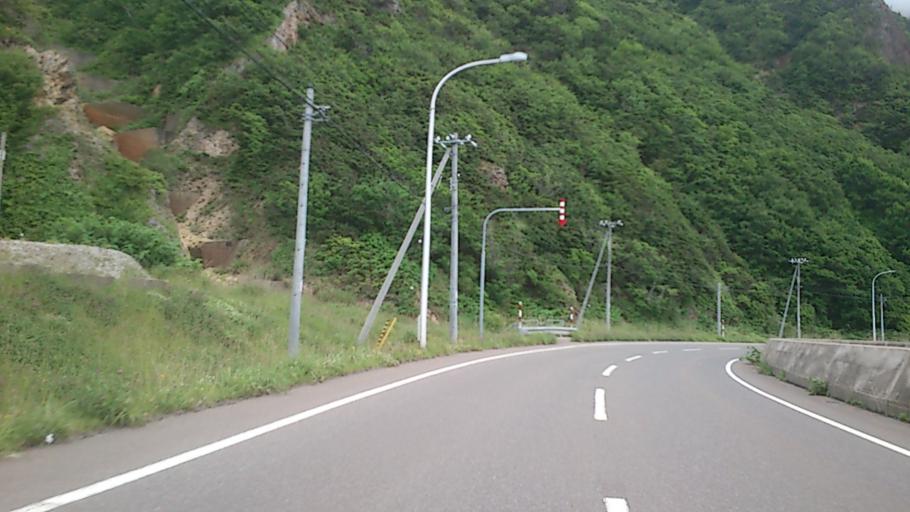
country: JP
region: Hokkaido
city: Kamiiso
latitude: 42.2758
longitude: 139.7854
